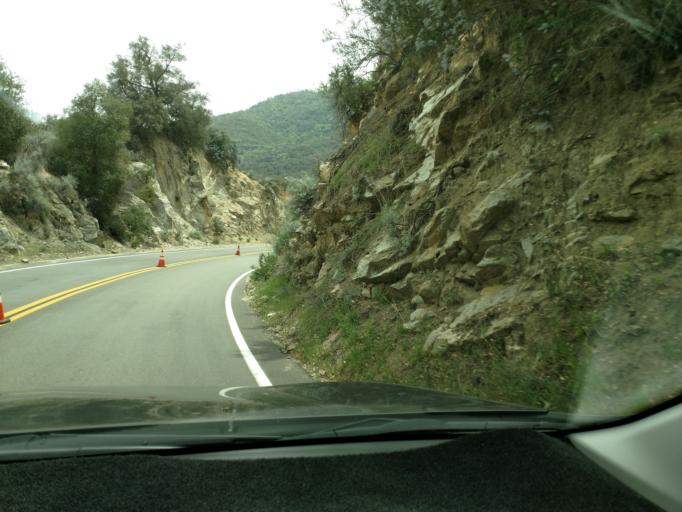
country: US
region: California
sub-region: Riverside County
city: Aguanga
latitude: 33.2428
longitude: -116.7634
